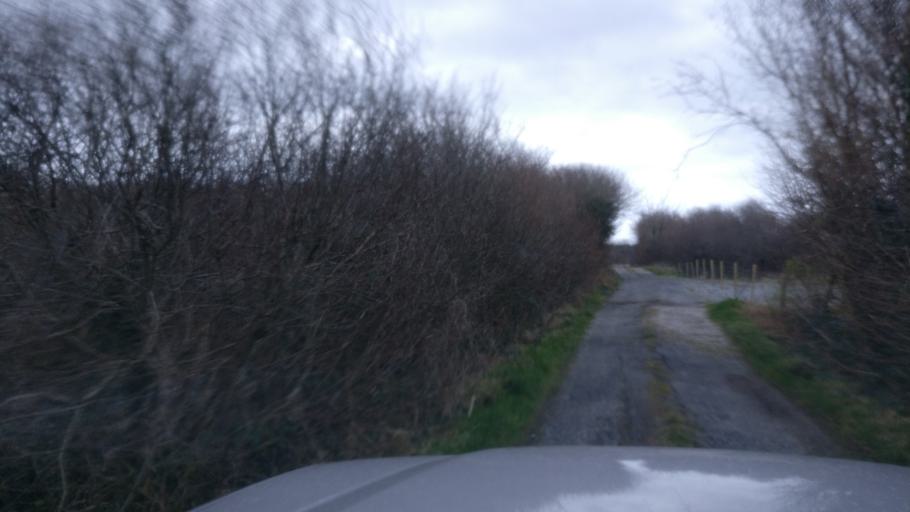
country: IE
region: Connaught
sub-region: County Galway
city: Loughrea
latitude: 53.2741
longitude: -8.4557
